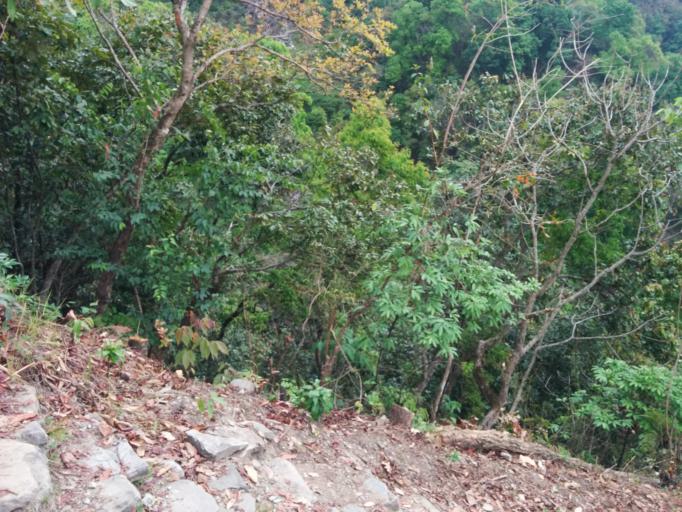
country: NP
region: Western Region
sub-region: Gandaki Zone
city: Pokhara
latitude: 28.2334
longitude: 83.9492
